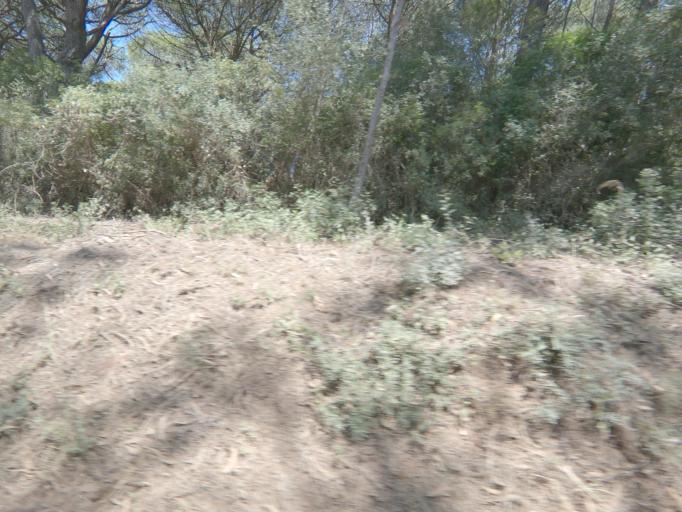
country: PT
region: Setubal
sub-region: Setubal
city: Setubal
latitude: 38.5115
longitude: -8.9291
